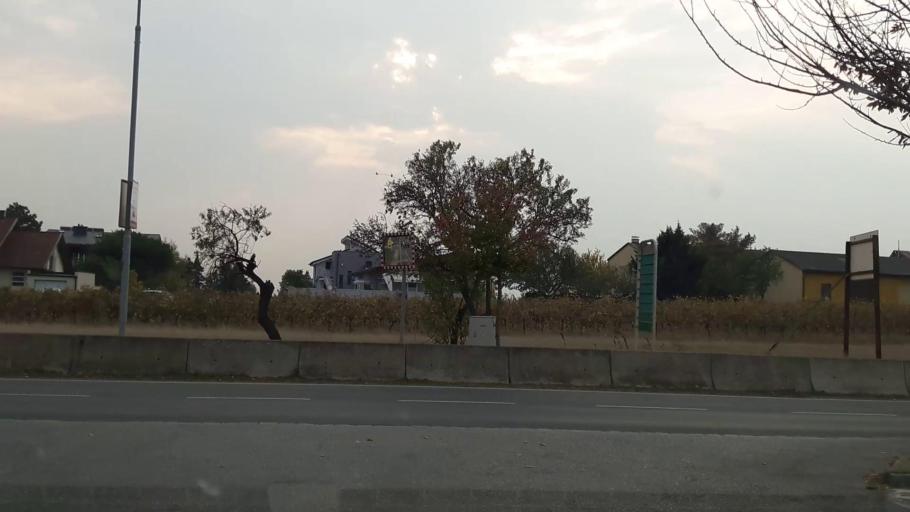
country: AT
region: Burgenland
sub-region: Politischer Bezirk Neusiedl am See
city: Gols
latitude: 47.9047
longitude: 16.8993
